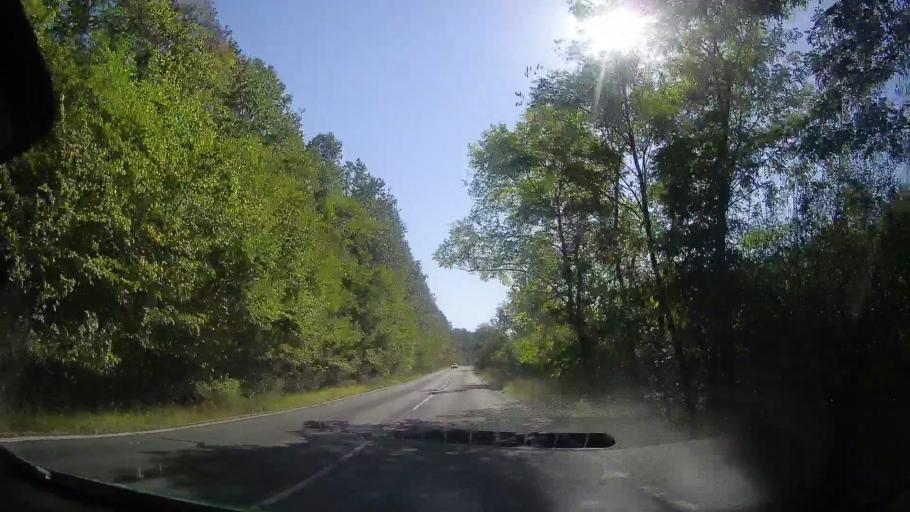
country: RO
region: Timis
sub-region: Comuna Barna
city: Barna
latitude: 45.7387
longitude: 21.9965
